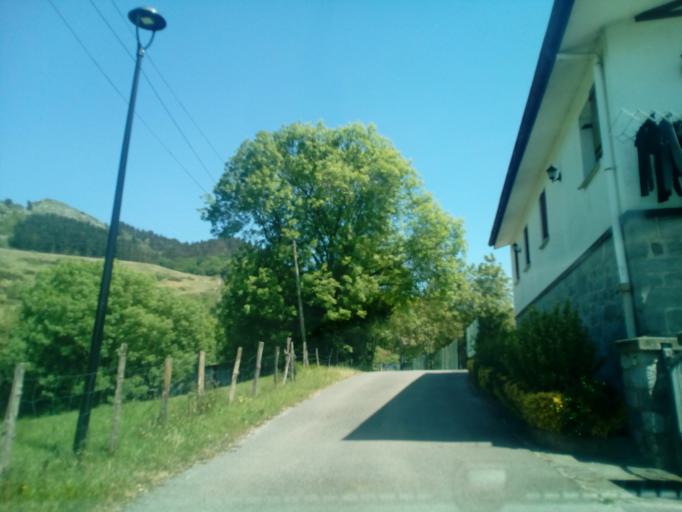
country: ES
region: Basque Country
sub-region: Provincia de Guipuzcoa
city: Andoain
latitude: 43.2264
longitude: -2.0168
